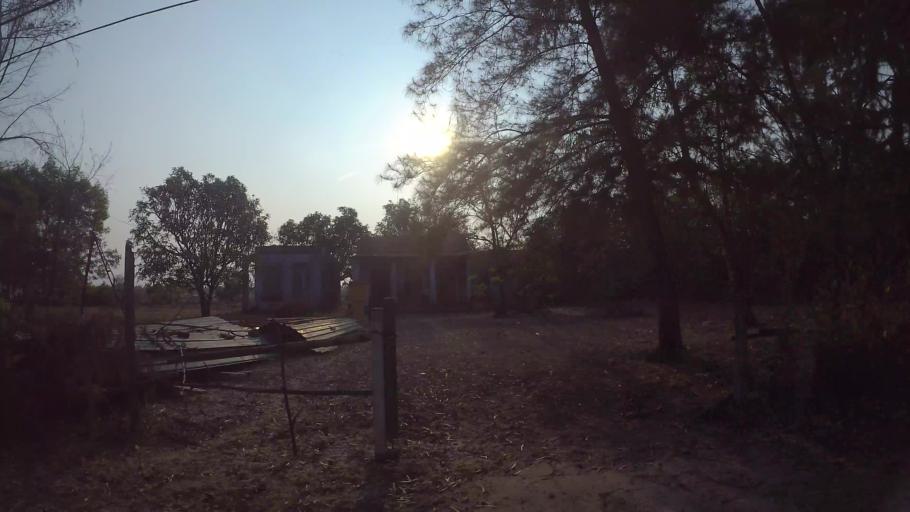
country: VN
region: Da Nang
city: Ngu Hanh Son
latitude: 15.9708
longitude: 108.2440
